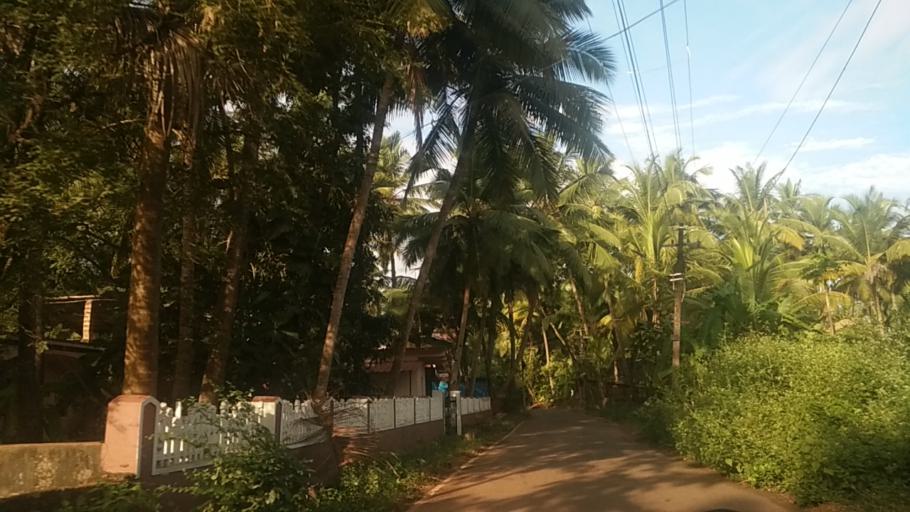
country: IN
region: Goa
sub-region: South Goa
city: Cuncolim
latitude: 15.1812
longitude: 73.9676
